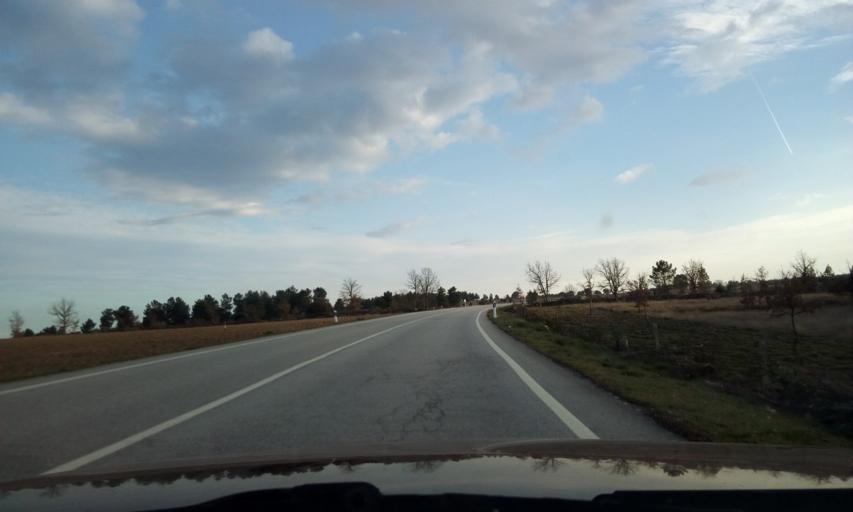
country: PT
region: Guarda
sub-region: Pinhel
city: Pinhel
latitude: 40.6573
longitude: -6.9668
